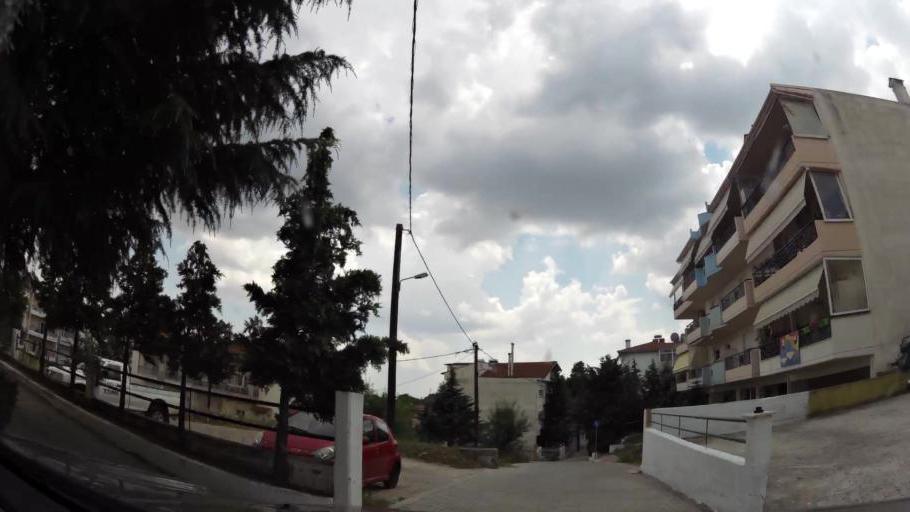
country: GR
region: West Macedonia
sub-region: Nomos Kozanis
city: Kozani
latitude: 40.2986
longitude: 21.8005
